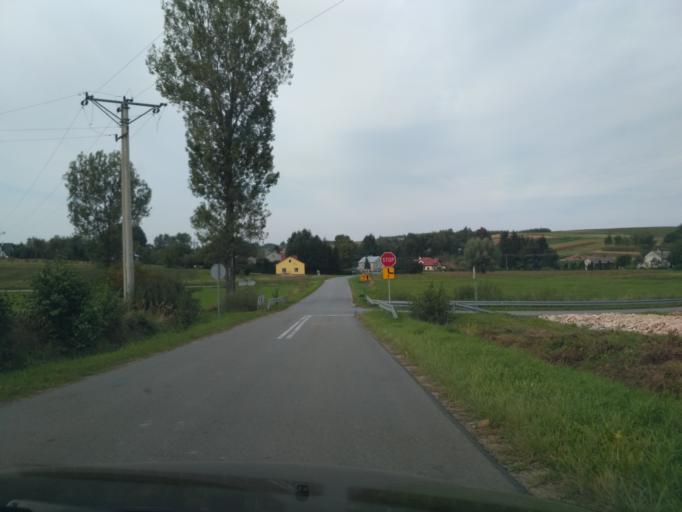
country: PL
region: Subcarpathian Voivodeship
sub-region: Powiat rzeszowski
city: Zglobien
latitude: 50.0316
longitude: 21.8437
